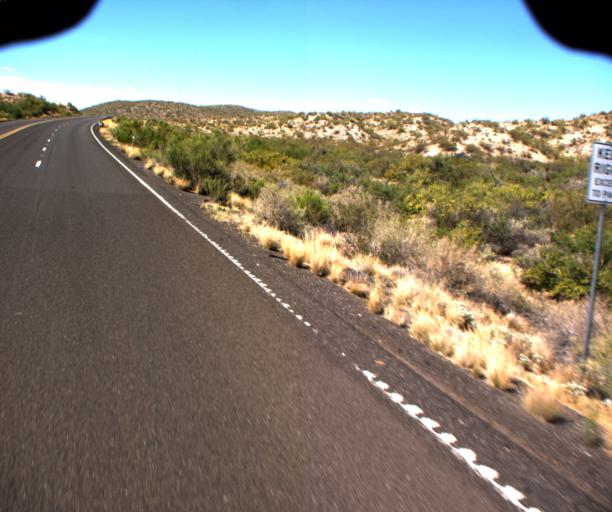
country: US
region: Arizona
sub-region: Mohave County
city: Kingman
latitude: 34.9243
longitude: -113.6584
